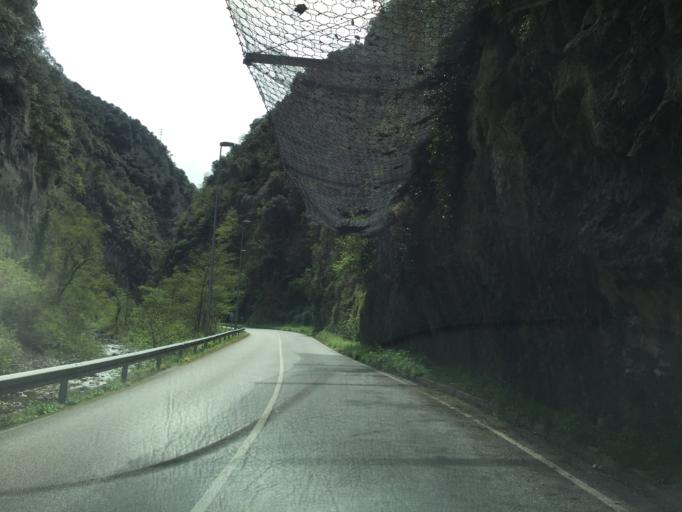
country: ES
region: Asturias
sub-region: Province of Asturias
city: Proaza
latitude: 43.2343
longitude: -6.0322
